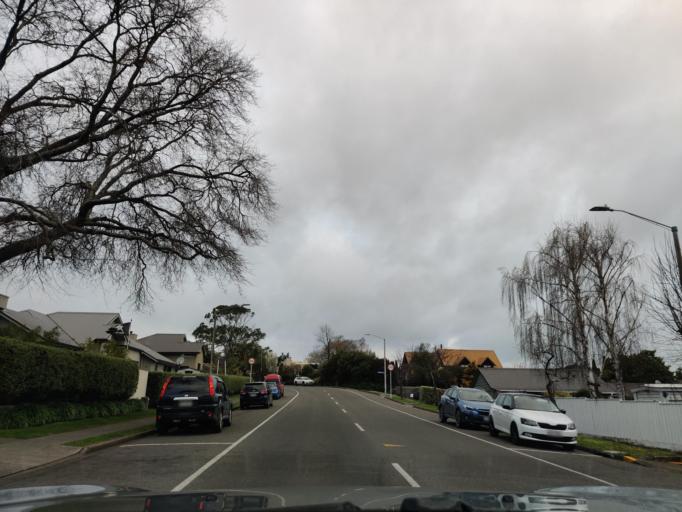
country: NZ
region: Hawke's Bay
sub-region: Hastings District
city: Hastings
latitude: -39.6690
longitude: 176.8814
